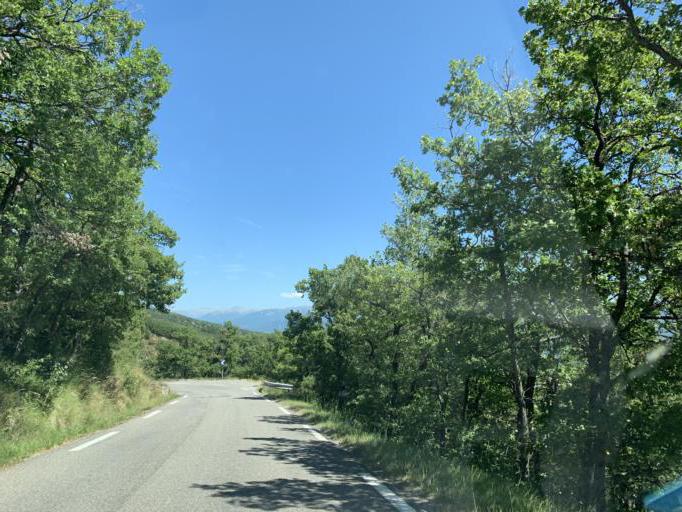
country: FR
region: Provence-Alpes-Cote d'Azur
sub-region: Departement des Hautes-Alpes
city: La Batie-Neuve
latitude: 44.5823
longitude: 6.1705
